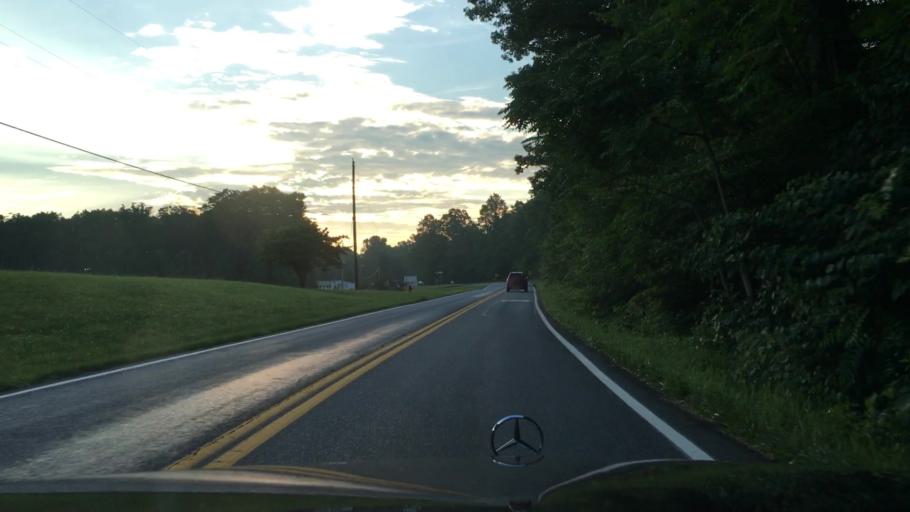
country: US
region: Virginia
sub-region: Campbell County
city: Timberlake
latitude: 37.2799
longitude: -79.2496
